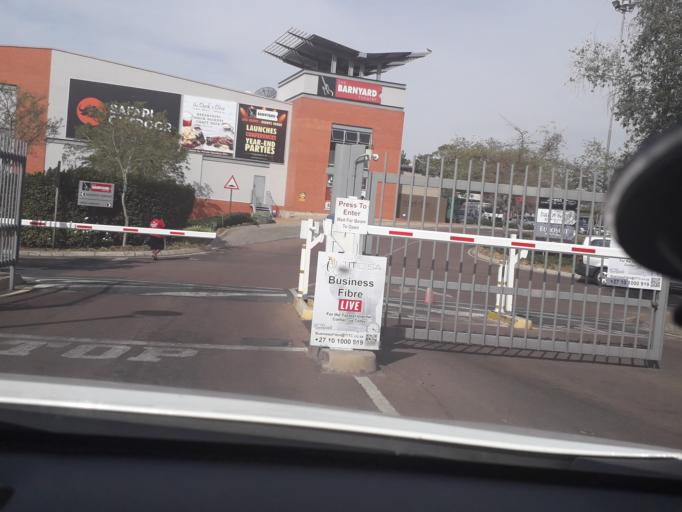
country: ZA
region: Gauteng
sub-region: City of Johannesburg Metropolitan Municipality
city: Midrand
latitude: -26.0364
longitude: 28.0587
